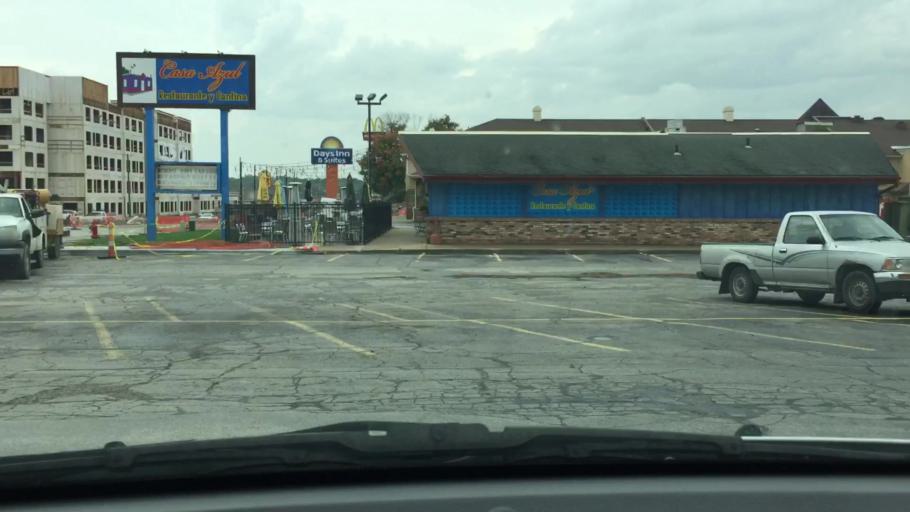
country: US
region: Iowa
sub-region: Johnson County
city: Coralville
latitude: 41.6799
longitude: -91.5663
